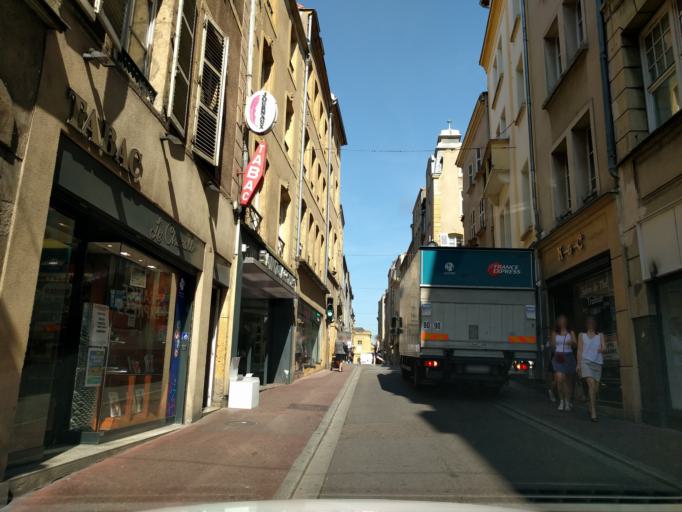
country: FR
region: Lorraine
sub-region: Departement de la Moselle
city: Metz
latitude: 49.1185
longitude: 6.1774
